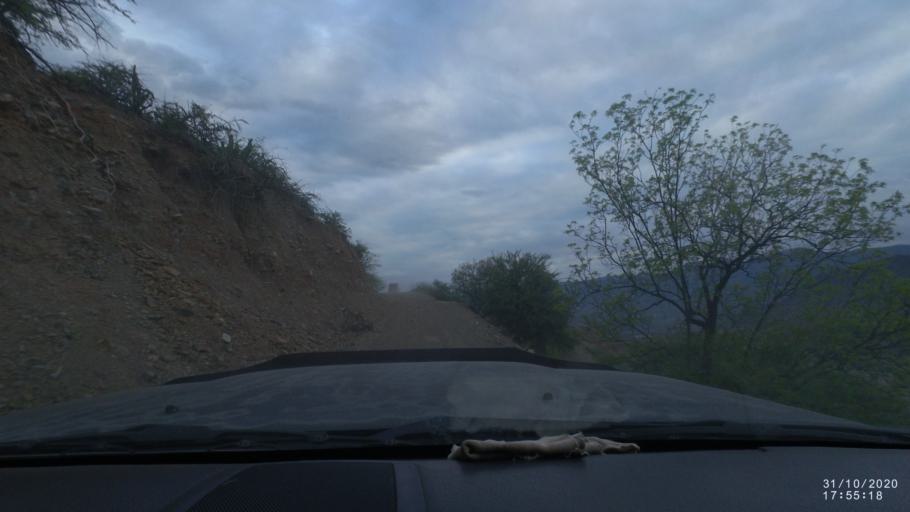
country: BO
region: Chuquisaca
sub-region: Provincia Zudanez
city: Mojocoya
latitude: -18.6435
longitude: -64.5280
